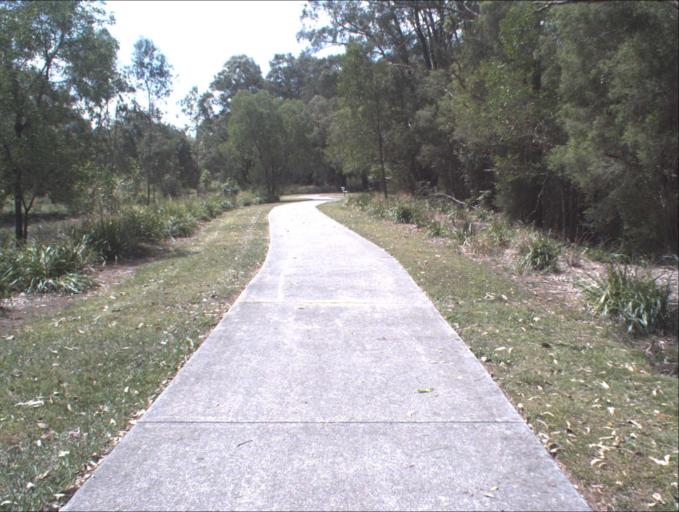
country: AU
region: Queensland
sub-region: Logan
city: Slacks Creek
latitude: -27.6697
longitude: 153.1594
